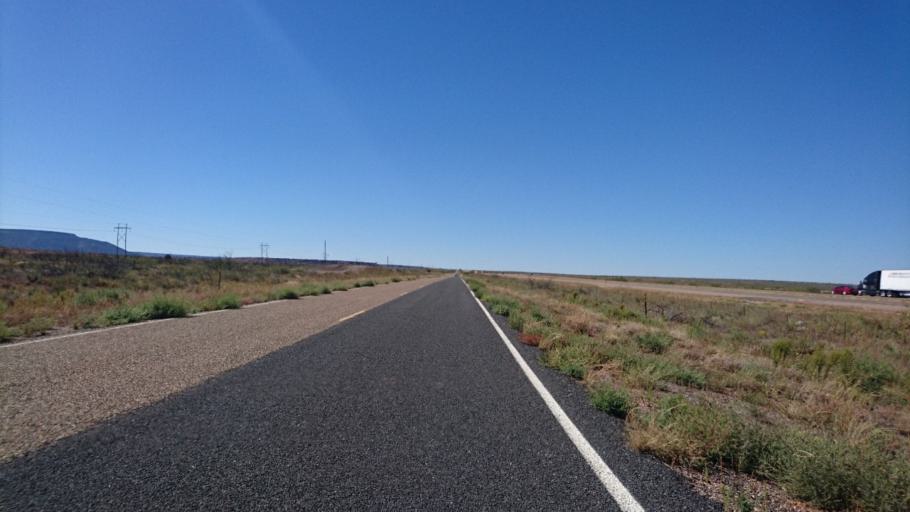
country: US
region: New Mexico
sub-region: Quay County
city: Tucumcari
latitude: 35.0874
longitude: -104.0931
